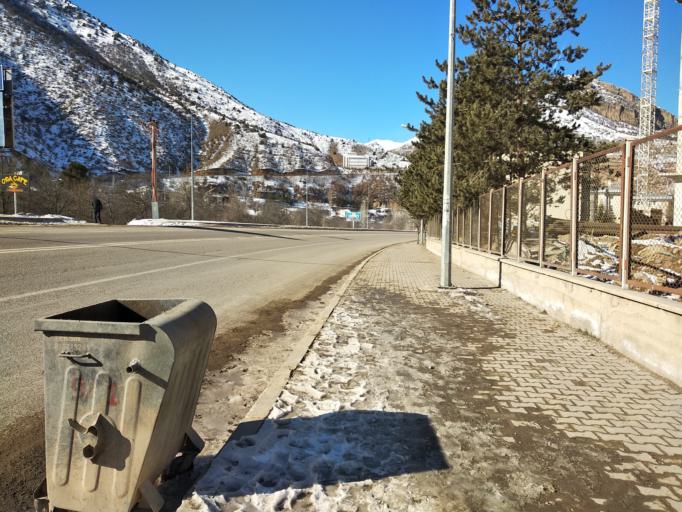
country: TR
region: Gumushane
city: Gumushkhane
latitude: 40.4367
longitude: 39.5084
